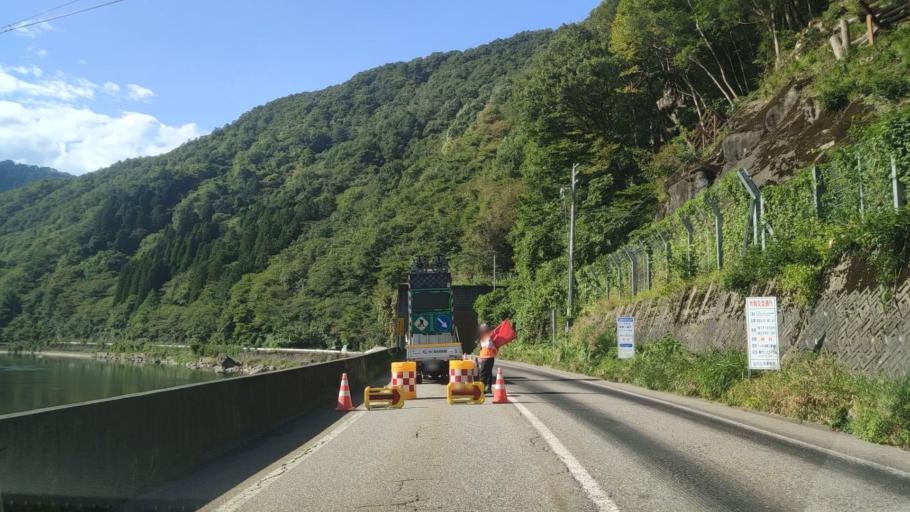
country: JP
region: Gifu
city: Takayama
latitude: 36.2785
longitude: 137.1352
